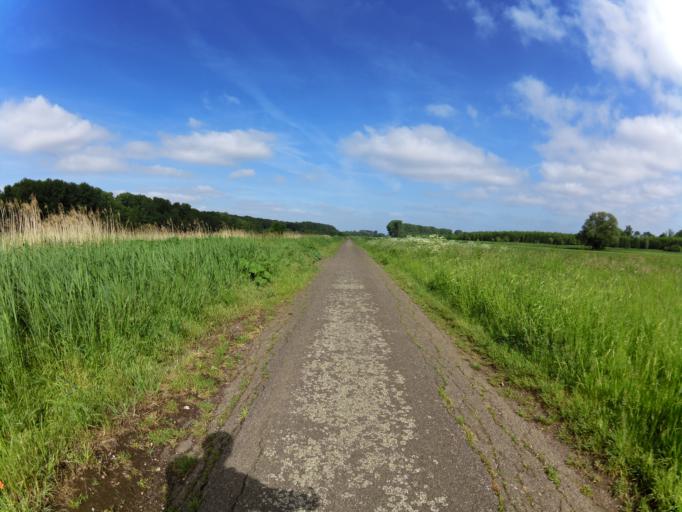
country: DE
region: North Rhine-Westphalia
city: Huckelhoven
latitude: 51.0212
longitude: 6.2090
